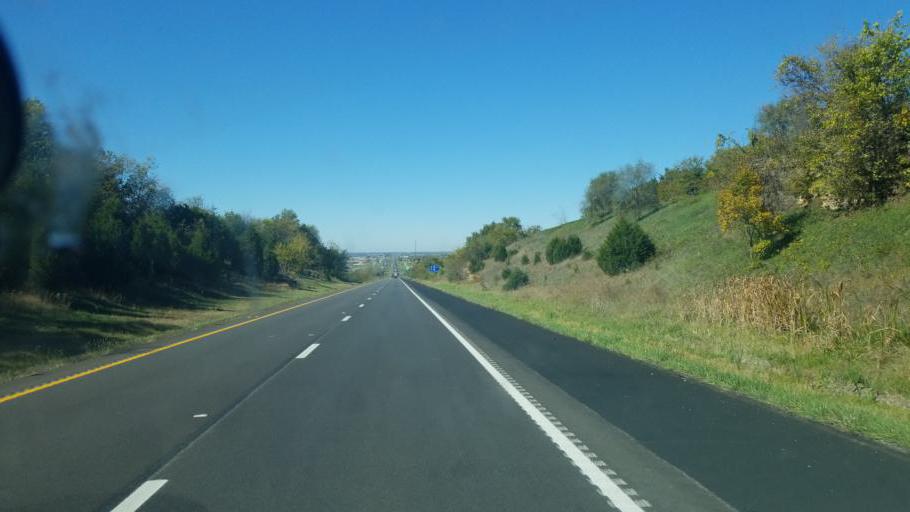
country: US
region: Missouri
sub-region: Lafayette County
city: Odessa
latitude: 39.0083
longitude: -93.9531
